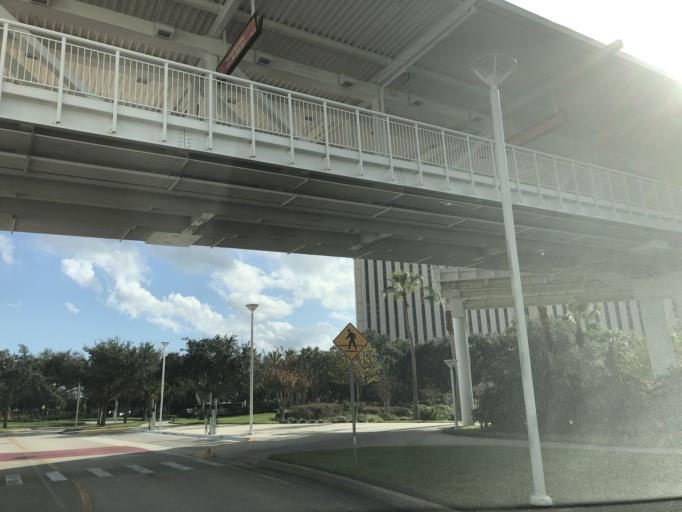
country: US
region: Florida
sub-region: Orange County
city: Williamsburg
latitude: 28.4270
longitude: -81.4642
